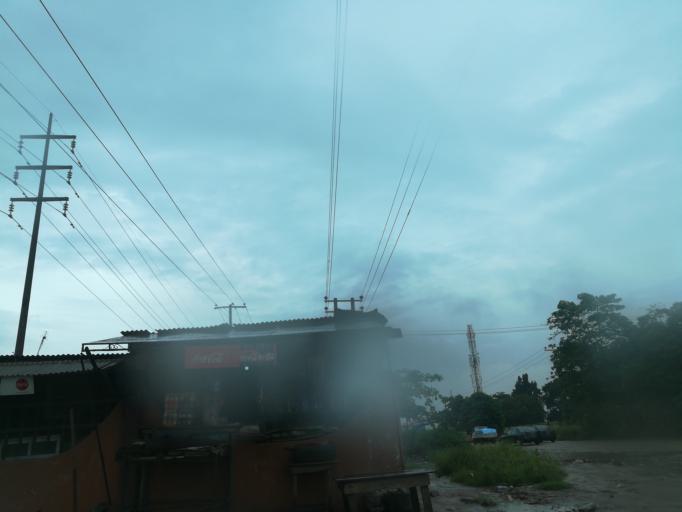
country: NG
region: Lagos
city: Ikorodu
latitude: 6.6357
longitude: 3.5125
